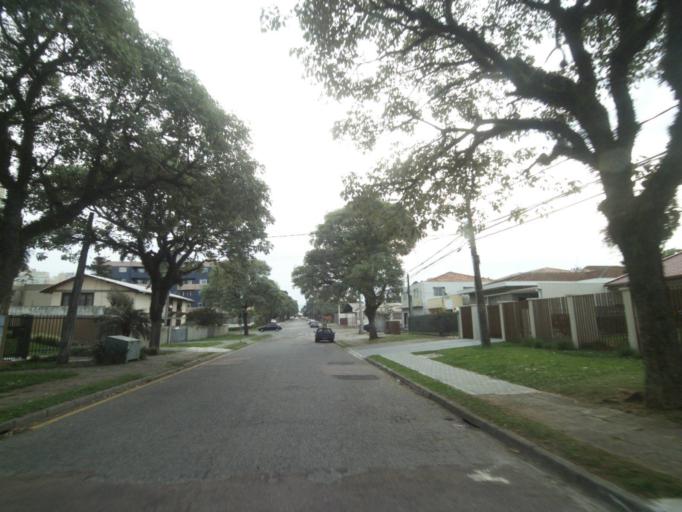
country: BR
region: Parana
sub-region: Curitiba
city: Curitiba
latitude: -25.4318
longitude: -49.2351
